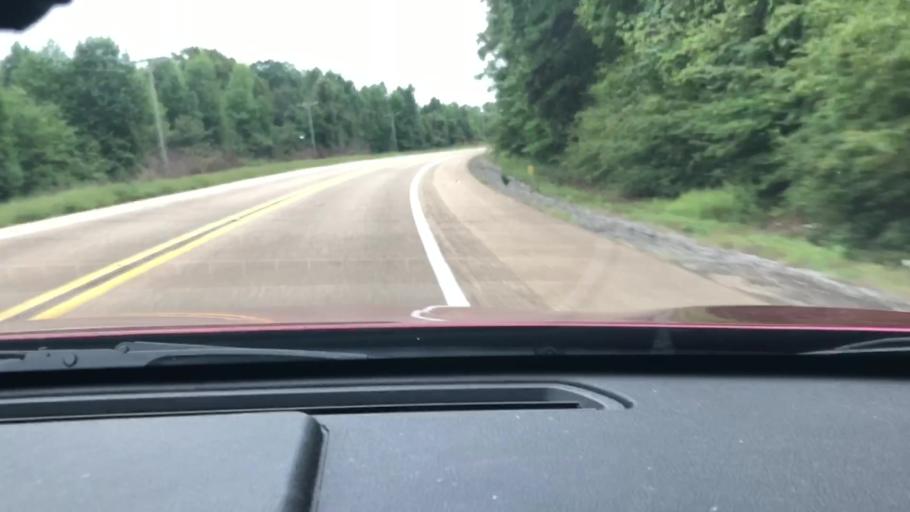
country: US
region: Arkansas
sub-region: Miller County
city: Texarkana
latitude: 33.4184
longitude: -93.8149
